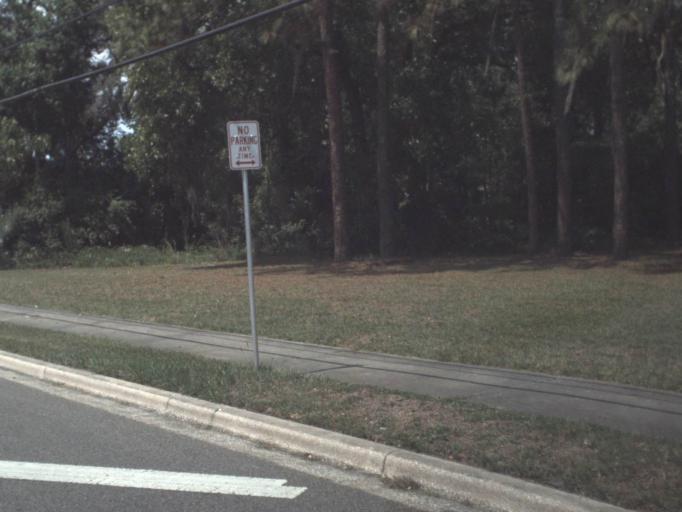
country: US
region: Florida
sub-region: Duval County
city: Jacksonville
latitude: 30.3553
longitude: -81.6036
